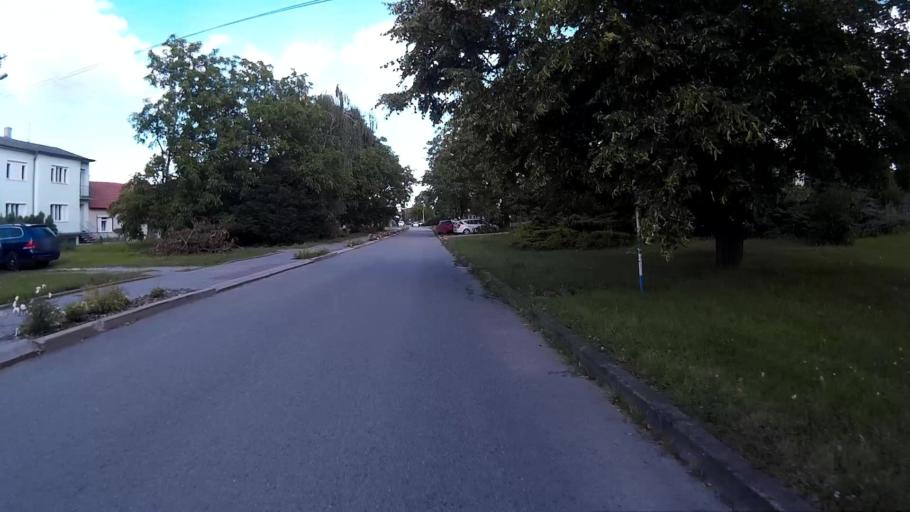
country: CZ
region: South Moravian
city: Tesany
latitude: 49.0429
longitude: 16.7712
